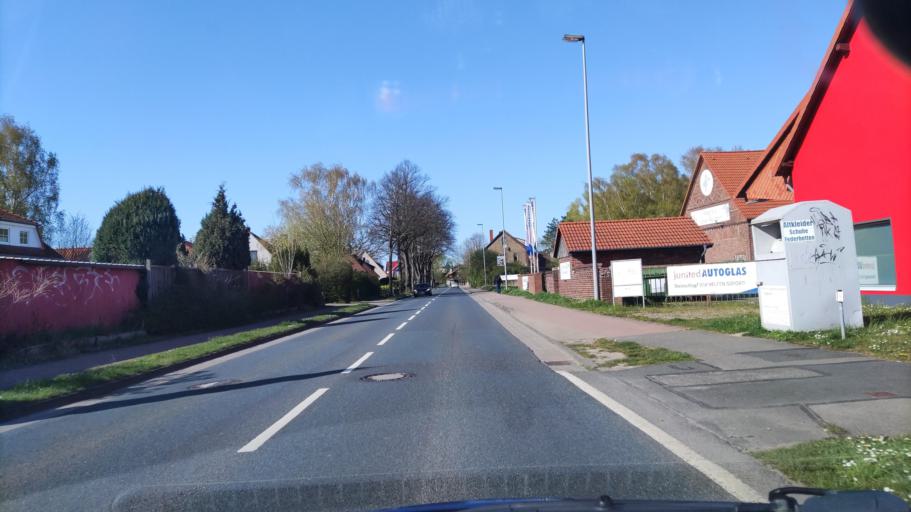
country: DE
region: Lower Saxony
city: Lehrte
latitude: 52.3655
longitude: 9.9763
